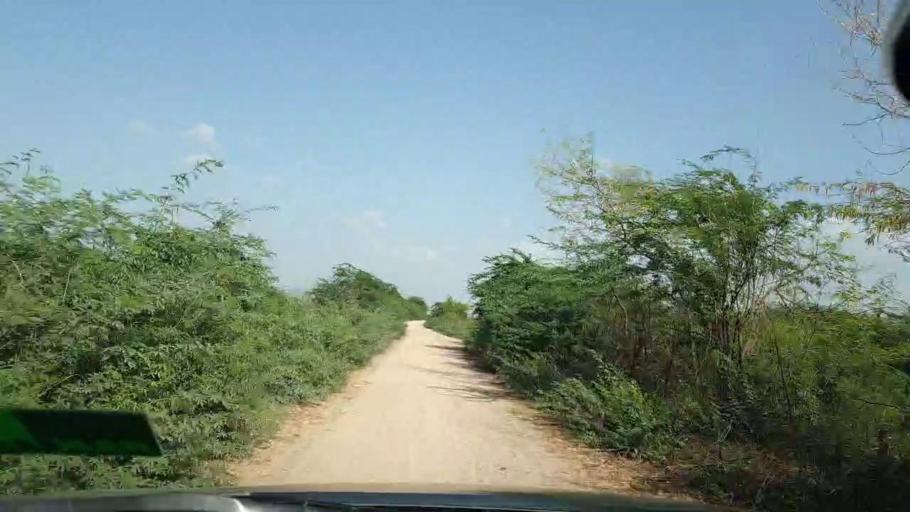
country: PK
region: Sindh
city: Tando Bago
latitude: 24.6827
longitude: 69.1988
